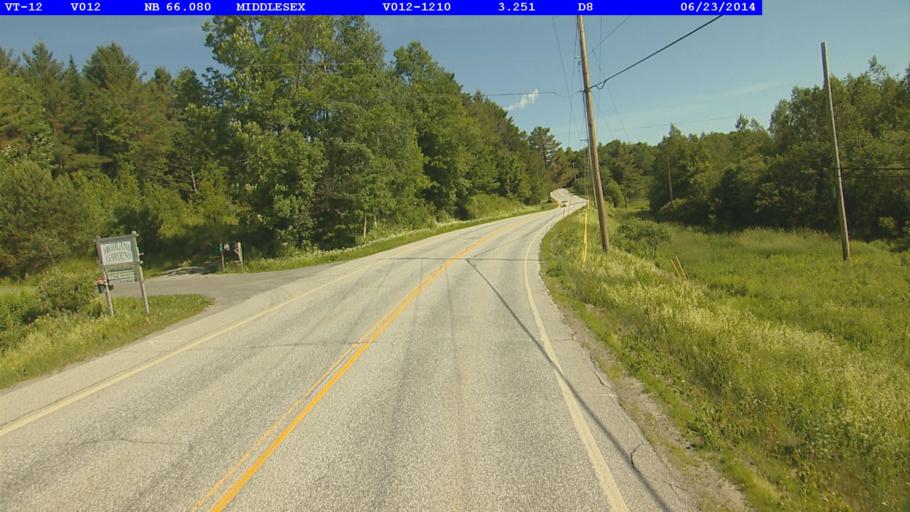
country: US
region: Vermont
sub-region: Washington County
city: Montpelier
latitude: 44.3471
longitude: -72.5660
